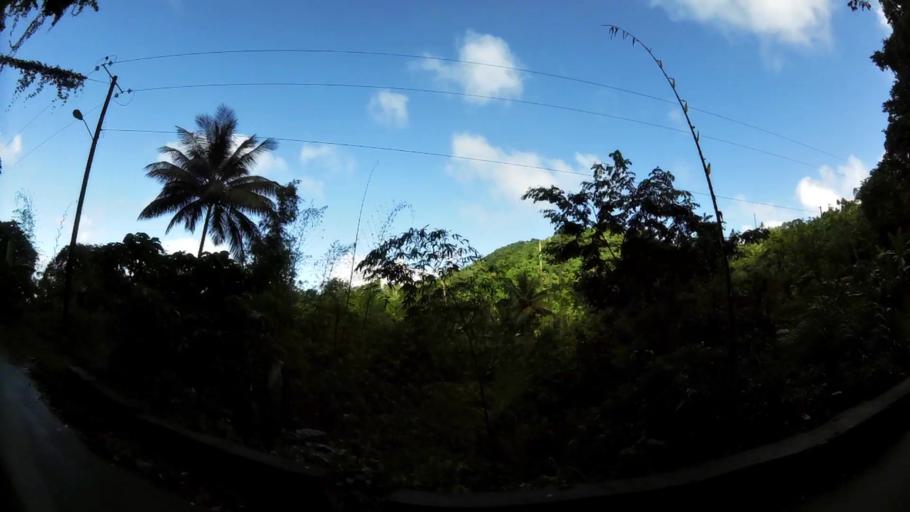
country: LC
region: Soufriere
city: Soufriere
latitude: 13.8714
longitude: -61.0429
